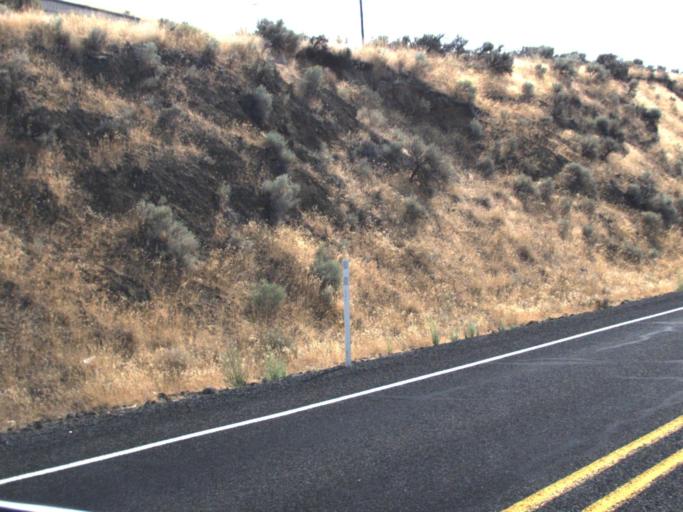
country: US
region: Washington
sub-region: Benton County
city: Prosser
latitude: 46.2019
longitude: -119.7582
